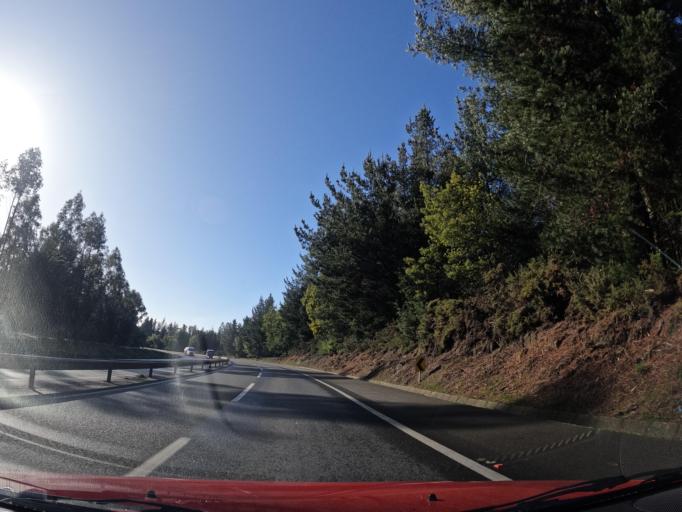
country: CL
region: Biobio
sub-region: Provincia de Concepcion
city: Penco
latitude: -36.7597
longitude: -72.9316
